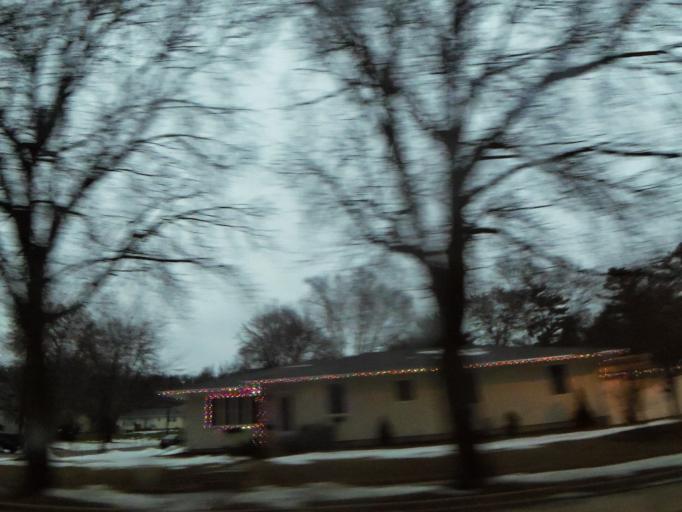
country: US
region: Minnesota
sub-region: Olmsted County
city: Rochester
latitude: 44.0362
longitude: -92.4698
